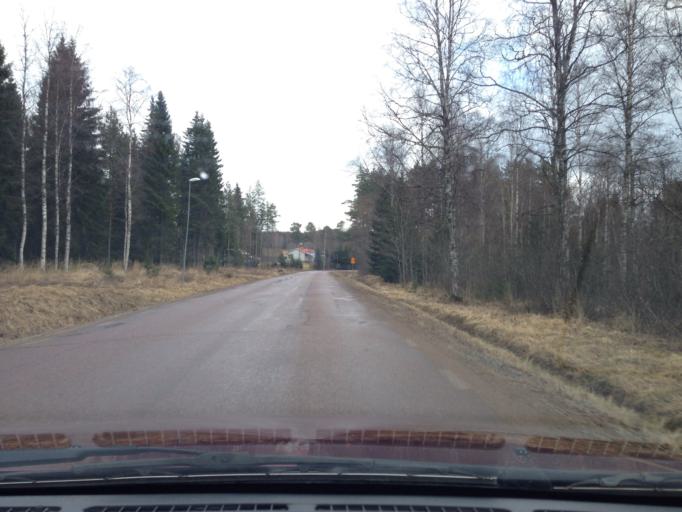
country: SE
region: Dalarna
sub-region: Smedjebackens Kommun
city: Smedjebacken
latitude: 60.1812
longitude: 15.3128
